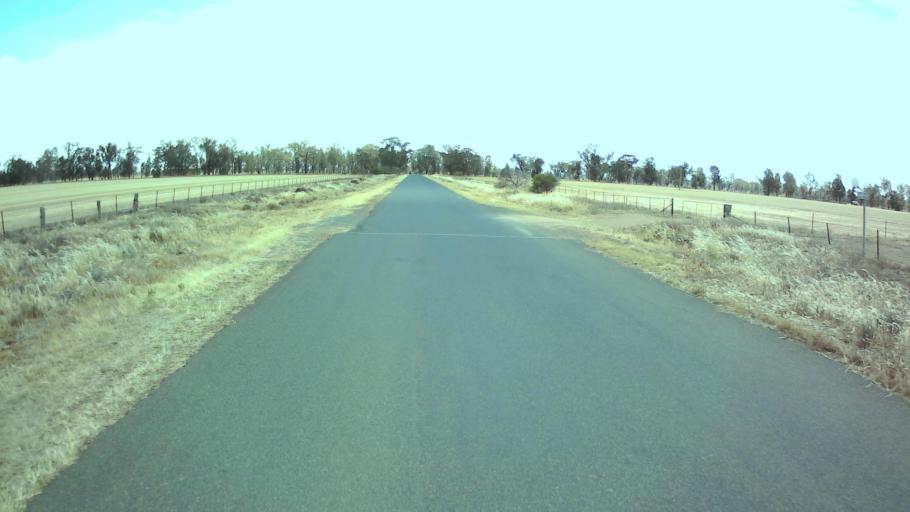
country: AU
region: New South Wales
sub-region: Weddin
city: Grenfell
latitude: -34.0720
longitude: 147.7773
